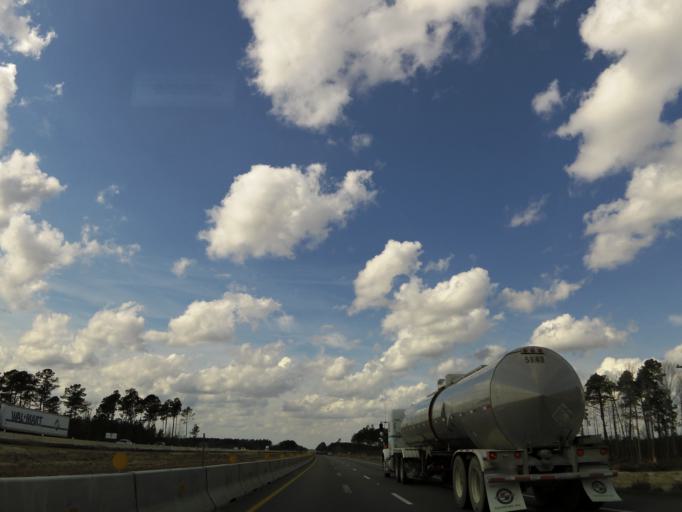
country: US
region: South Carolina
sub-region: Dorchester County
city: Summerville
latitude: 33.0557
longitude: -80.1671
